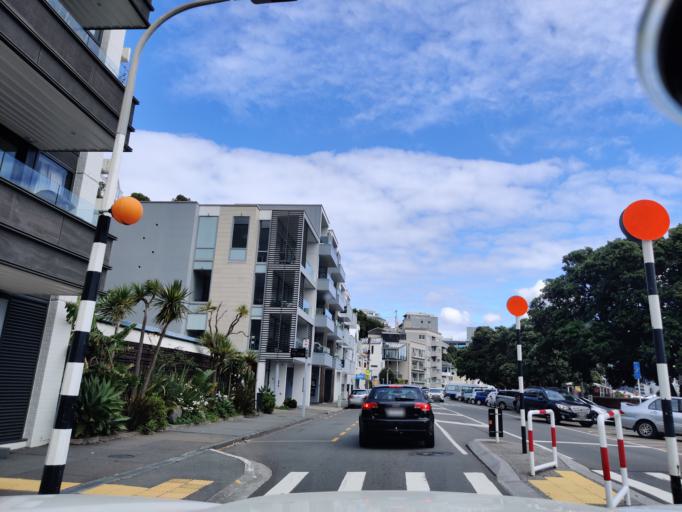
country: NZ
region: Wellington
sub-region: Wellington City
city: Wellington
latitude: -41.2911
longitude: 174.7901
